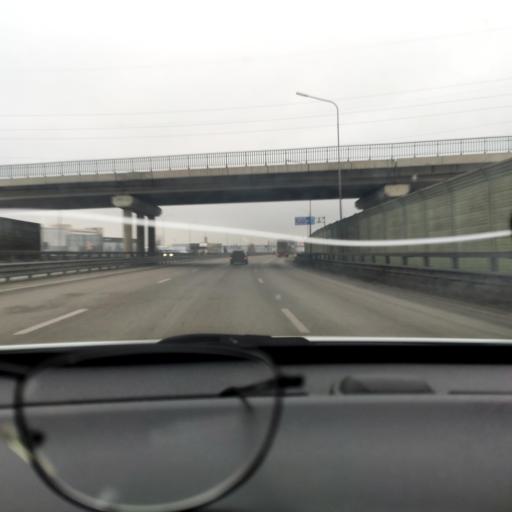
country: RU
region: Voronezj
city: Somovo
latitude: 51.6673
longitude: 39.3007
